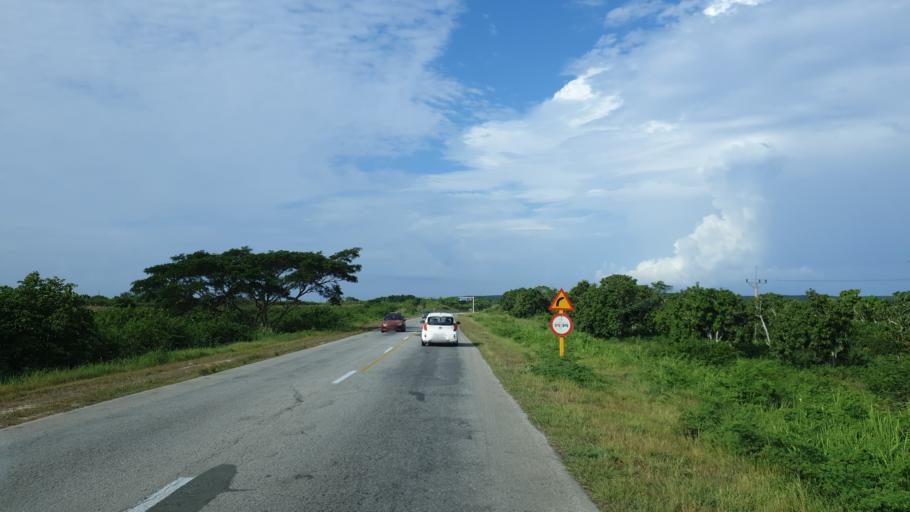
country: CU
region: Cienfuegos
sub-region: Municipio de Cienfuegos
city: Cienfuegos
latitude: 22.0800
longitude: -80.3889
